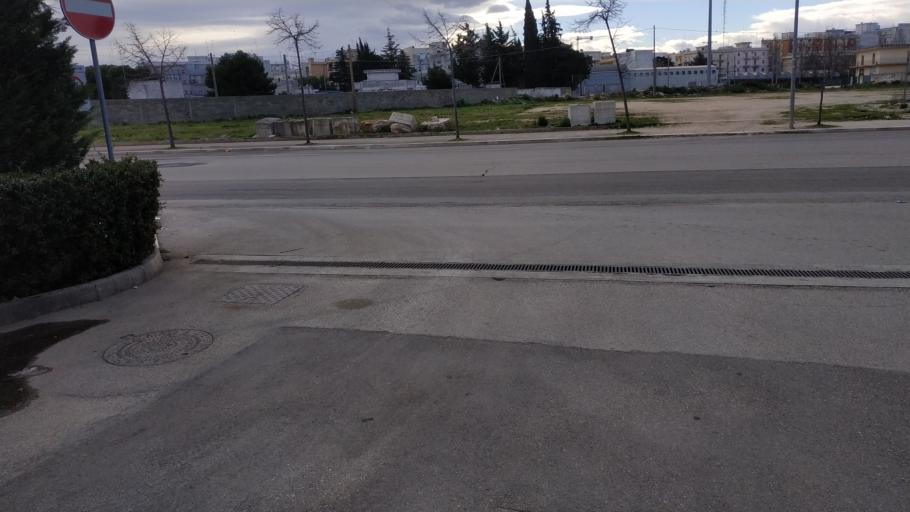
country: IT
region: Apulia
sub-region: Provincia di Bari
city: Bitonto
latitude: 41.1158
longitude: 16.6862
